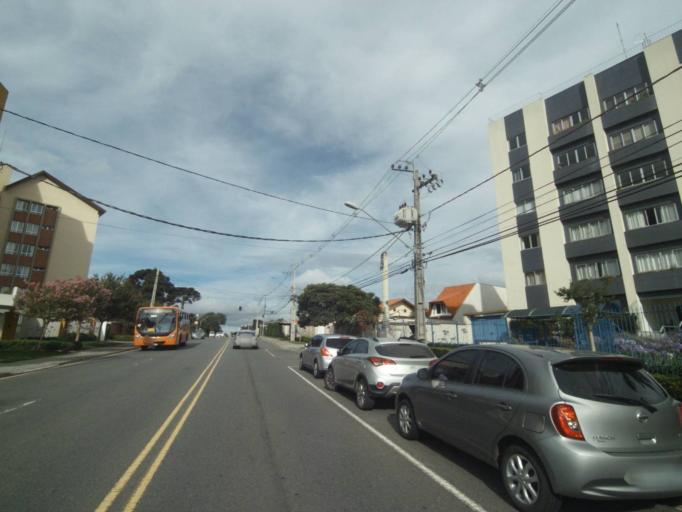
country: BR
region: Parana
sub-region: Curitiba
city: Curitiba
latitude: -25.4376
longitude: -49.3045
